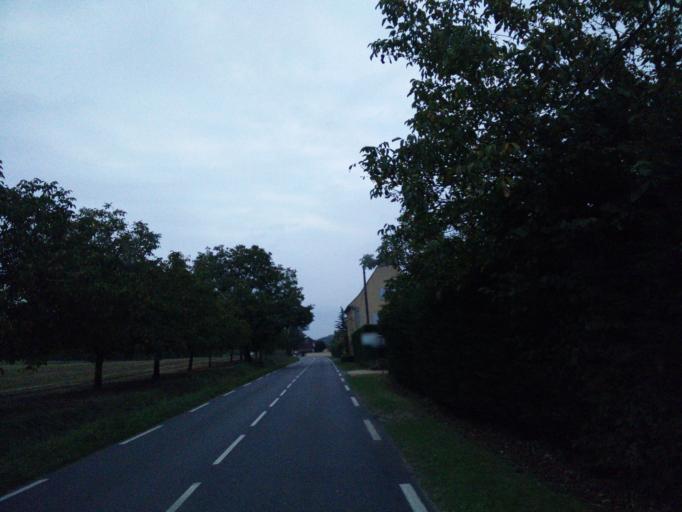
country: FR
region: Aquitaine
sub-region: Departement de la Dordogne
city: Carsac-Aillac
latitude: 44.8308
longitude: 1.2767
